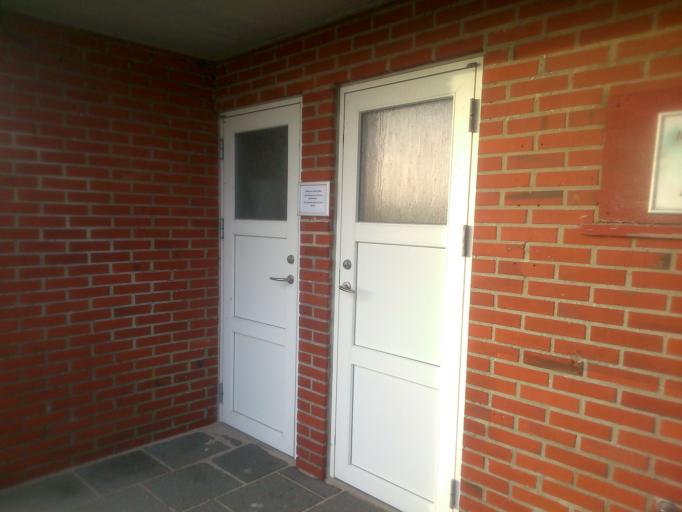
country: DK
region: Central Jutland
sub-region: Ringkobing-Skjern Kommune
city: Hvide Sande
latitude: 55.8166
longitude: 8.1758
